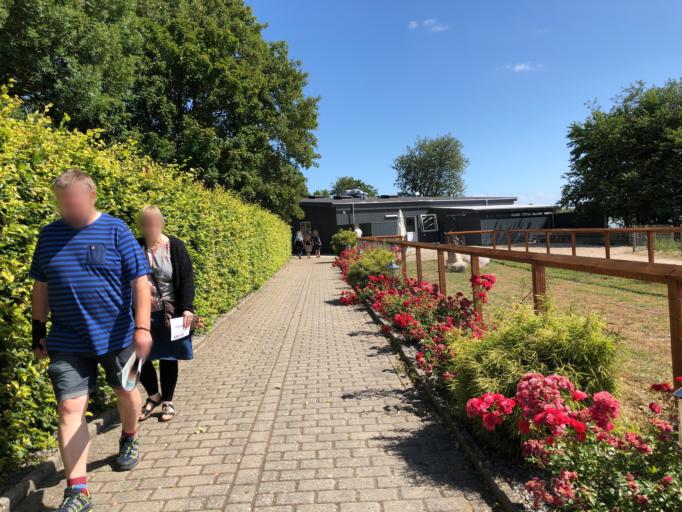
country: DK
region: North Denmark
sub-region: Mariagerfjord Kommune
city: Hobro
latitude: 56.5901
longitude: 9.6402
